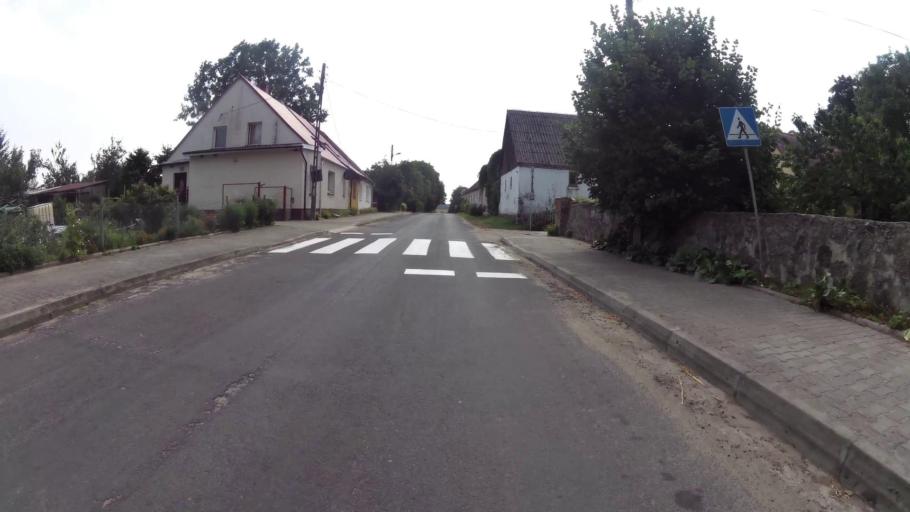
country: PL
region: West Pomeranian Voivodeship
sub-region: Powiat gryfinski
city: Moryn
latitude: 52.8553
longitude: 14.4221
